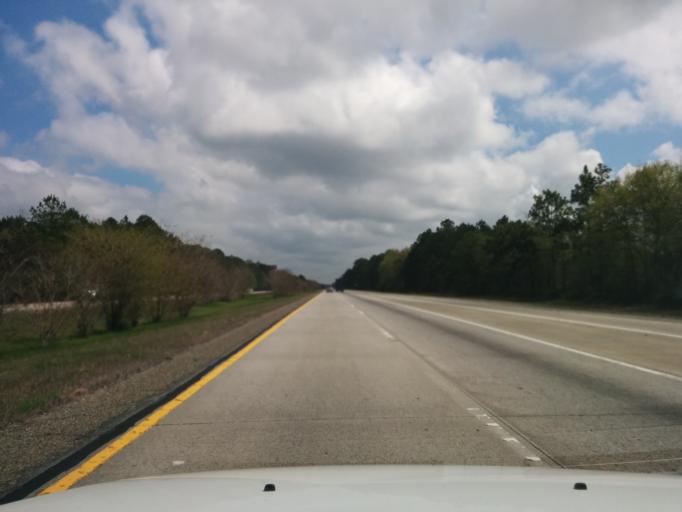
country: US
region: Georgia
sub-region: Bryan County
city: Pembroke
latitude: 32.2184
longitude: -81.5352
